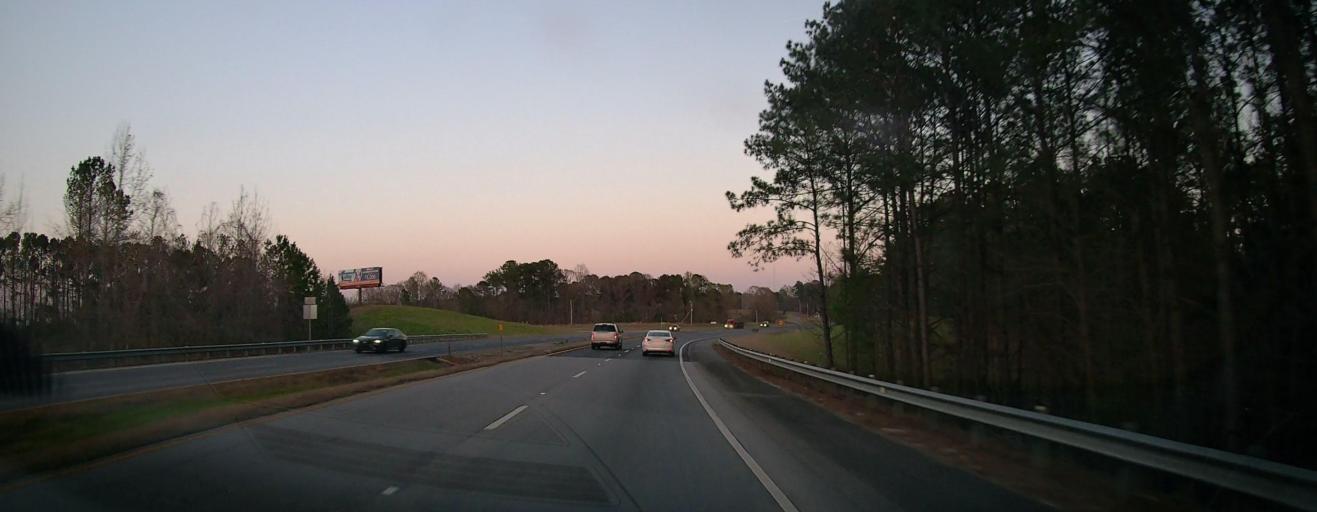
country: US
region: Alabama
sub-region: Tallapoosa County
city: Alexander City
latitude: 32.9063
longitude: -85.9033
